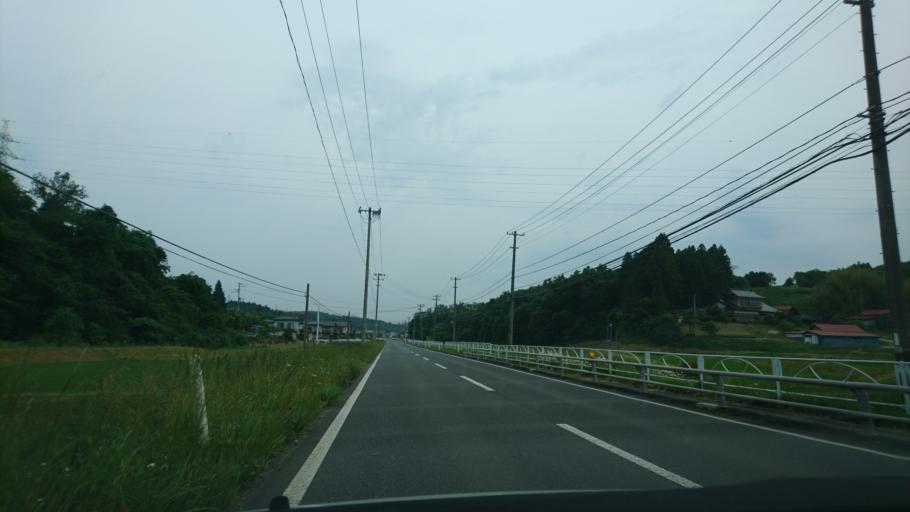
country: JP
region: Iwate
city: Ichinoseki
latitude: 38.8926
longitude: 141.1318
